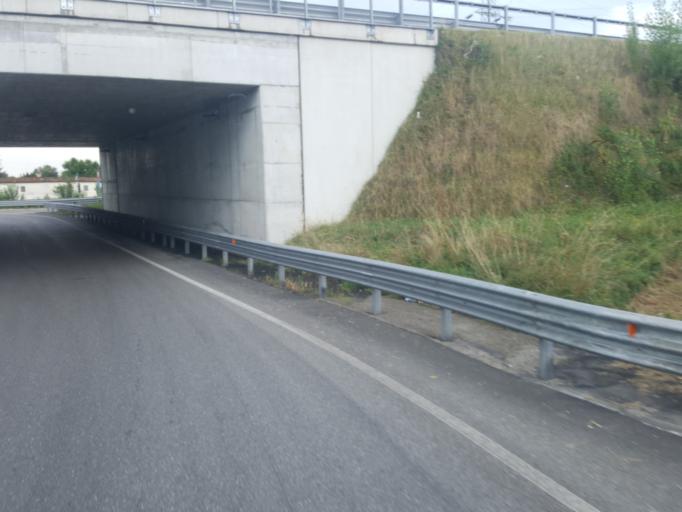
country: IT
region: Lombardy
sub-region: Provincia di Brescia
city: Roncadelle
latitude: 45.5293
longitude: 10.1690
